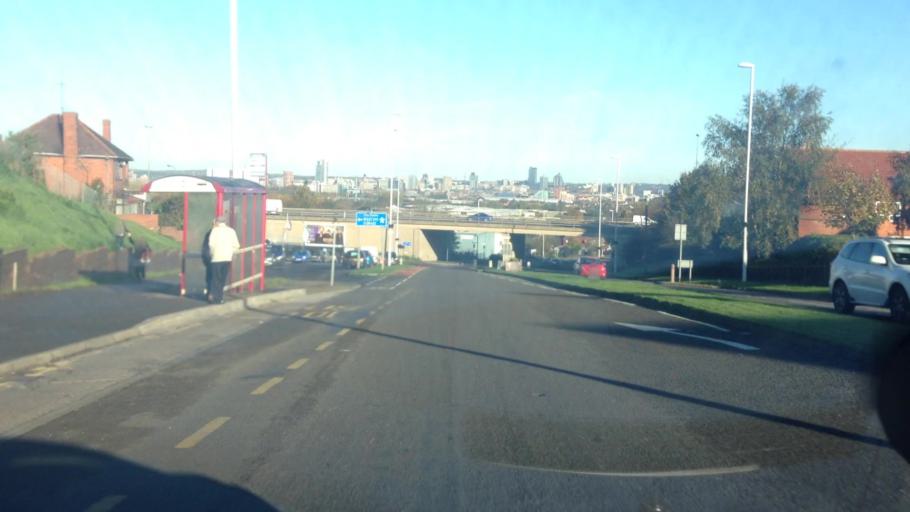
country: GB
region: England
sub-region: City and Borough of Leeds
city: Leeds
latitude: 53.7691
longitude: -1.5305
